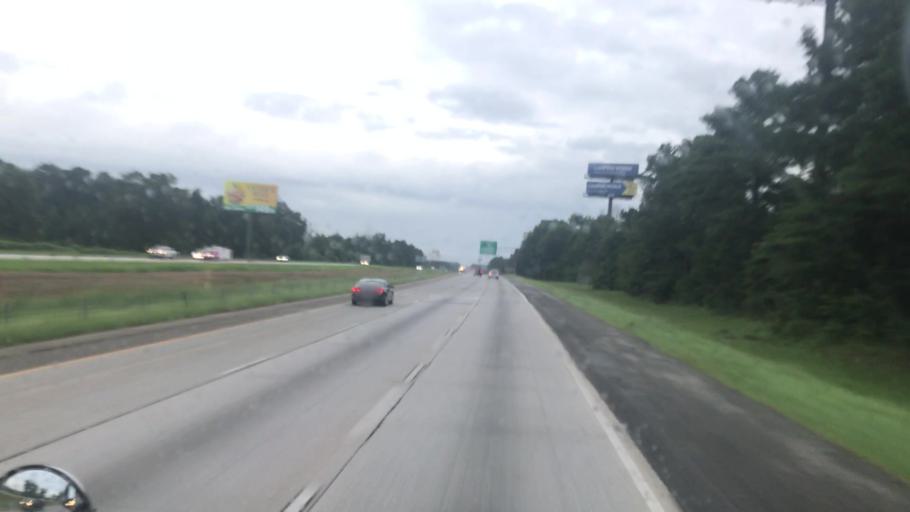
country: US
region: Georgia
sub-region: Peach County
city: Byron
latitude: 32.6008
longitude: -83.7423
